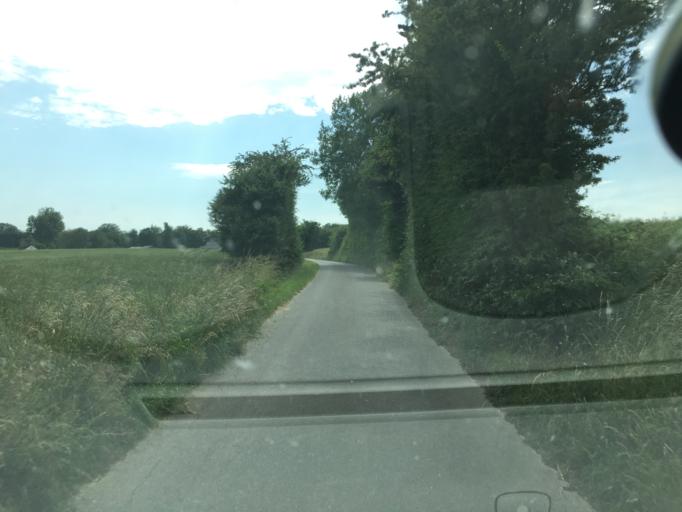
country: DK
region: South Denmark
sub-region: Sonderborg Kommune
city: Dybbol
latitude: 54.9345
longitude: 9.7367
